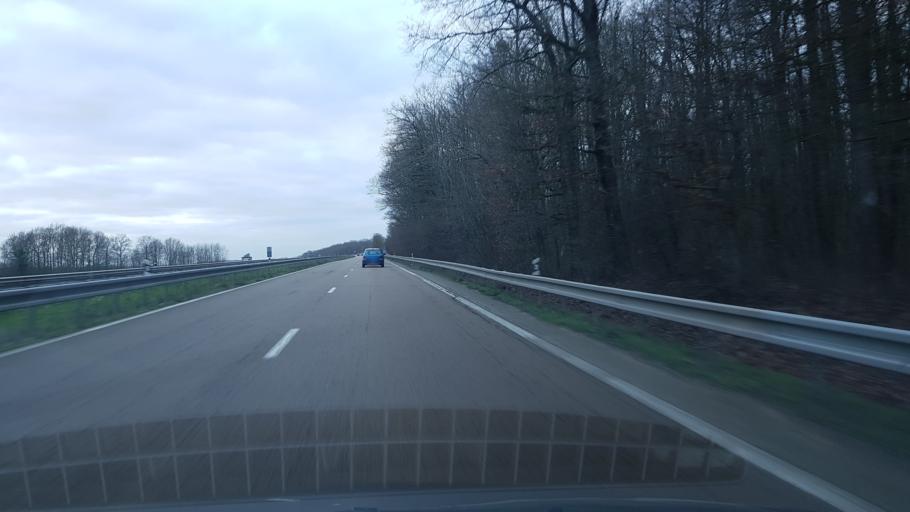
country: FR
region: Champagne-Ardenne
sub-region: Departement de la Marne
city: Esternay
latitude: 48.7317
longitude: 3.5941
